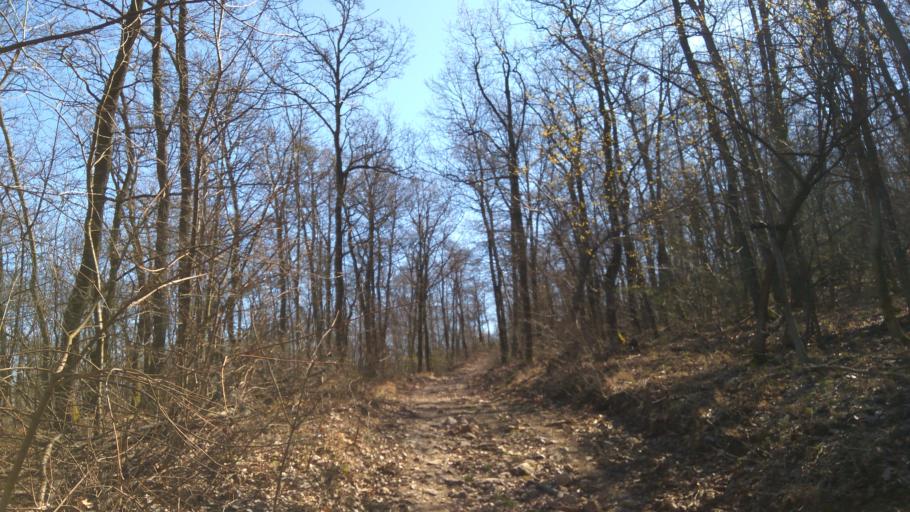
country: HU
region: Pest
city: Csobanka
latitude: 47.6370
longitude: 18.9790
